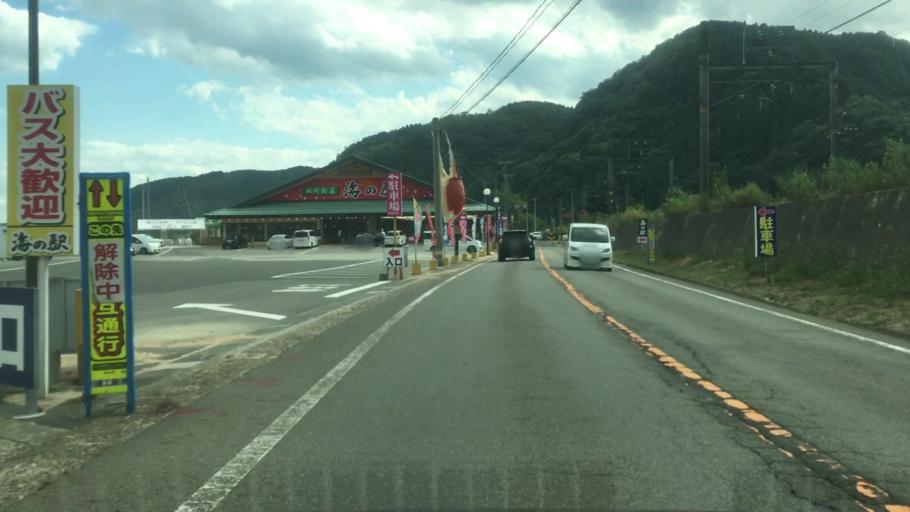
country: JP
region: Hyogo
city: Toyooka
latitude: 35.5941
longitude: 134.8009
